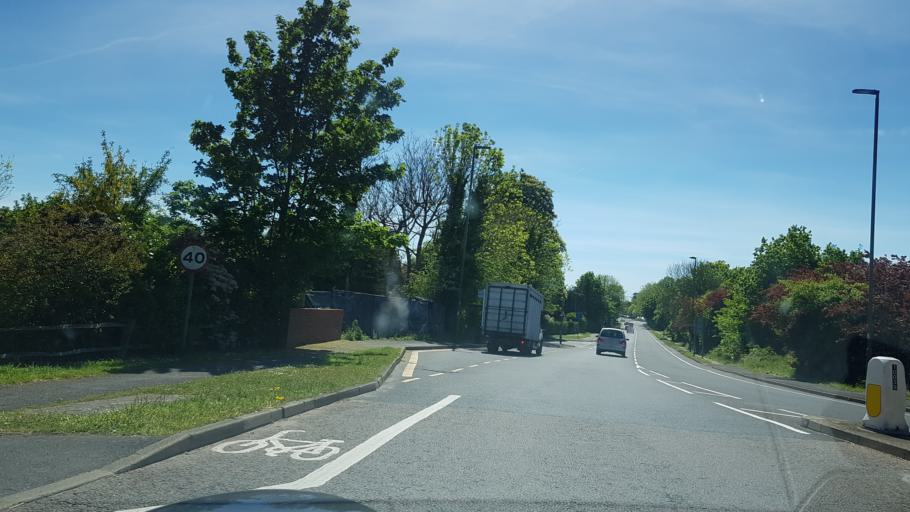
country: GB
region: England
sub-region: Surrey
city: Send
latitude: 51.2627
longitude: -0.5409
